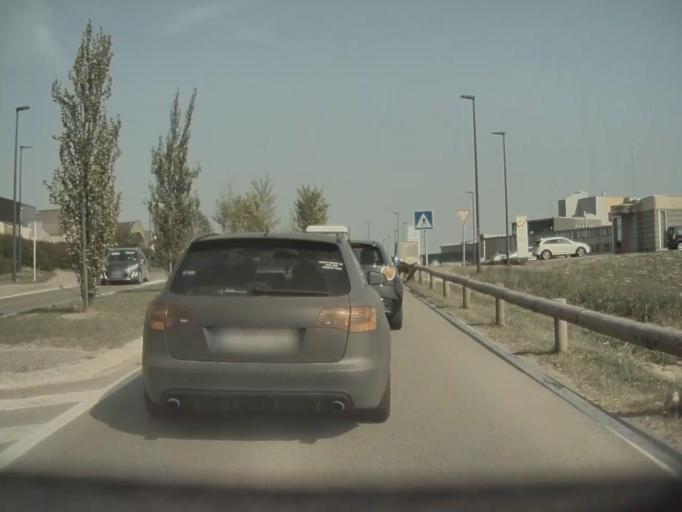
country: BE
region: Wallonia
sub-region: Province de Namur
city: Dinant
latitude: 50.2660
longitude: 4.9412
